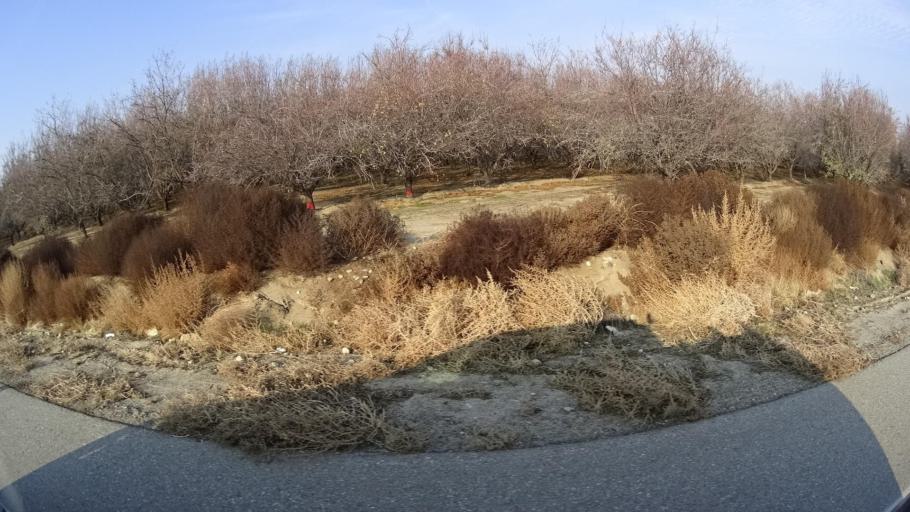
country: US
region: California
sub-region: Kern County
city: Arvin
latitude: 35.0407
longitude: -118.9201
